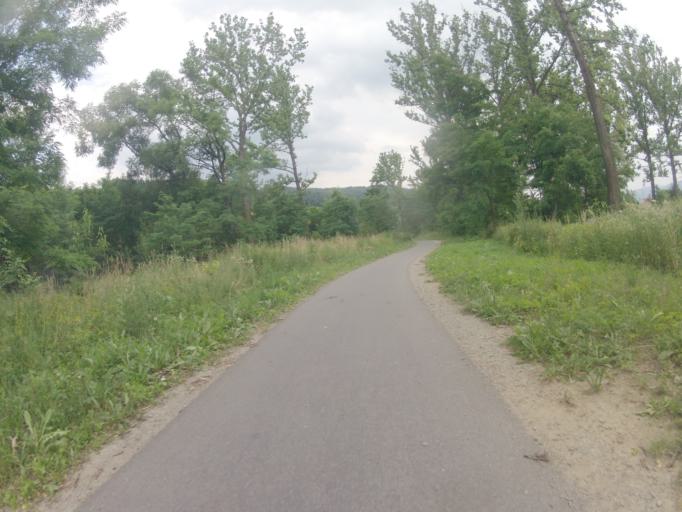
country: PL
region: Lesser Poland Voivodeship
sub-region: Powiat nowosadecki
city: Stary Sacz
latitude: 49.5369
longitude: 20.6585
